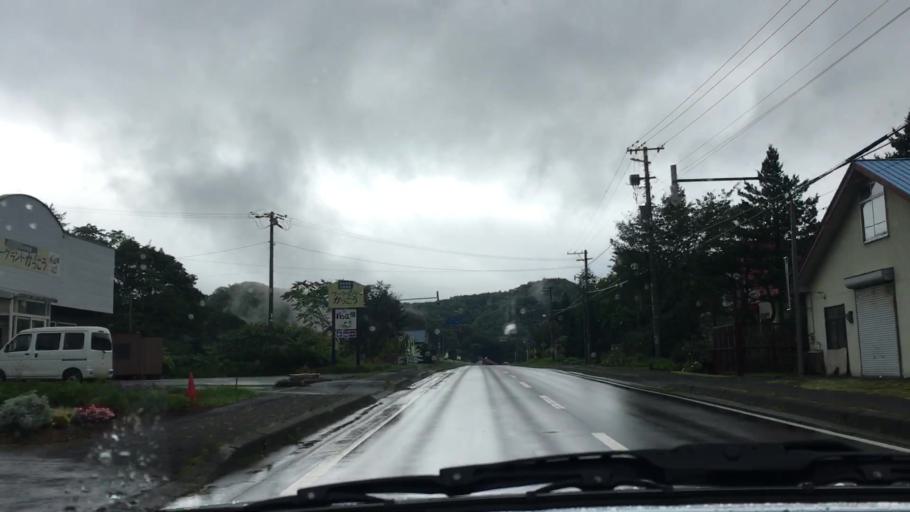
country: JP
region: Hokkaido
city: Niseko Town
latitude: 42.6440
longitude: 140.7330
